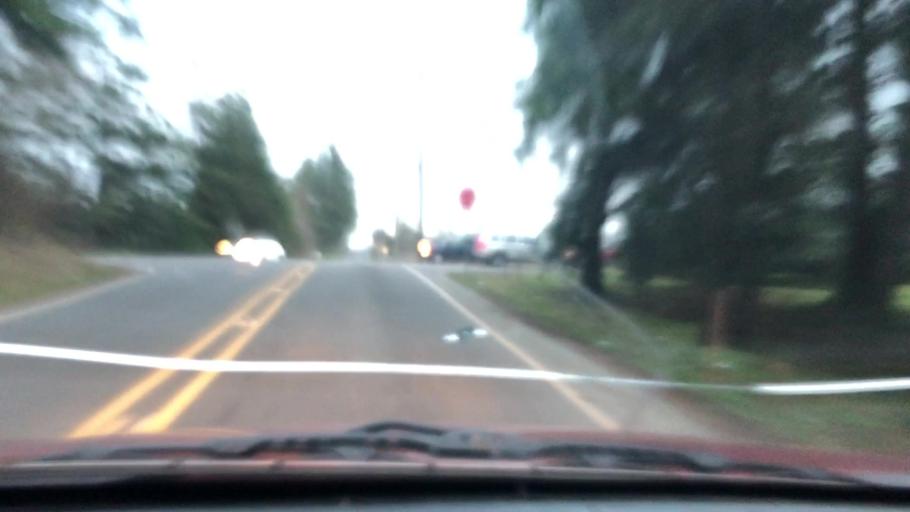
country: US
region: Washington
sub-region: Pierce County
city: Elk Plain
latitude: 47.0677
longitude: -122.4004
